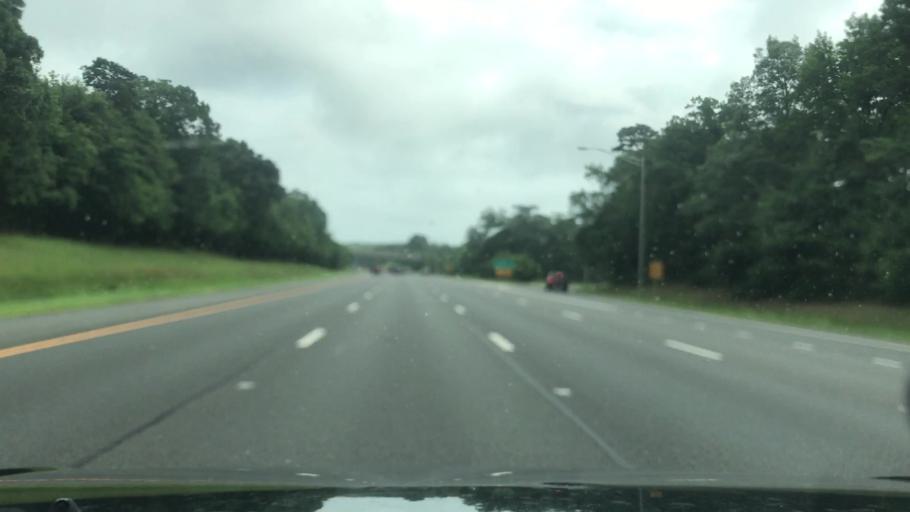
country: US
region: New Jersey
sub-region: Monmouth County
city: Shark River Hills
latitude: 40.2218
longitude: -74.0989
